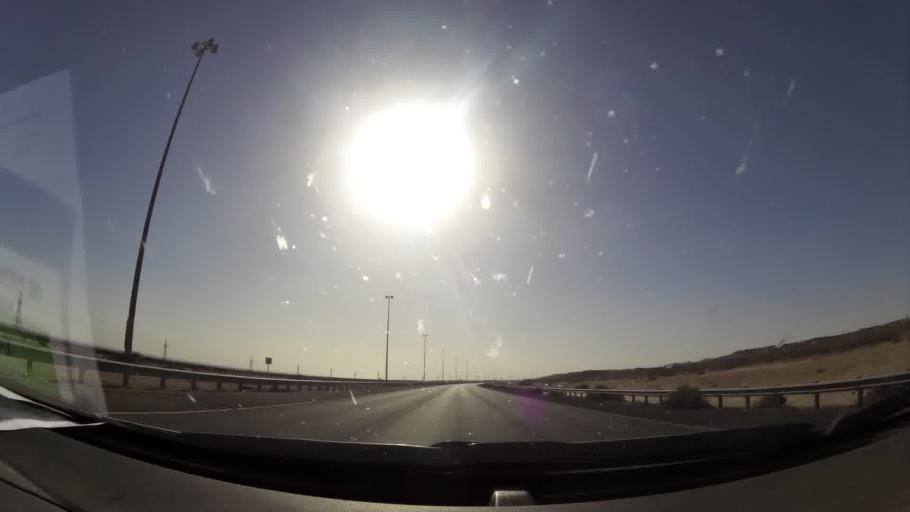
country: KW
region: Al Asimah
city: Kuwait City
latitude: 29.5536
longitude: 47.8782
